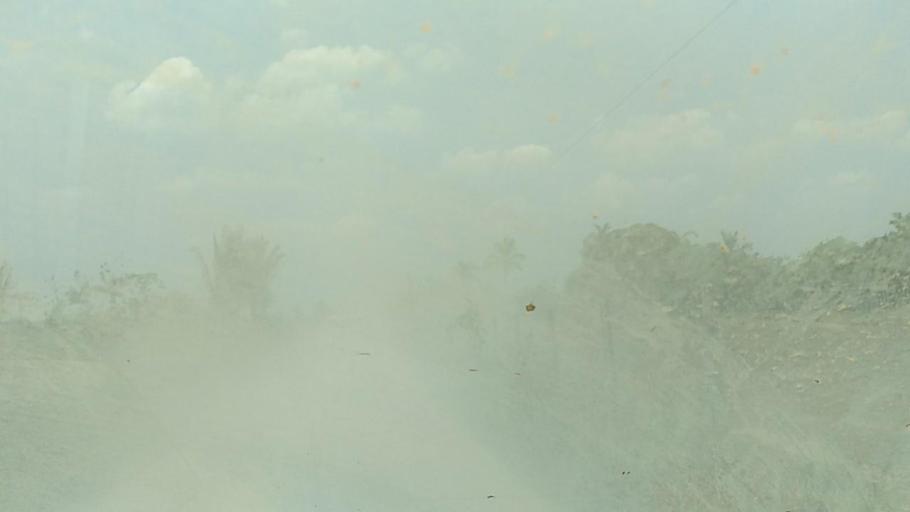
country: BR
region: Rondonia
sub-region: Porto Velho
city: Porto Velho
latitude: -8.7292
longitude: -63.3099
